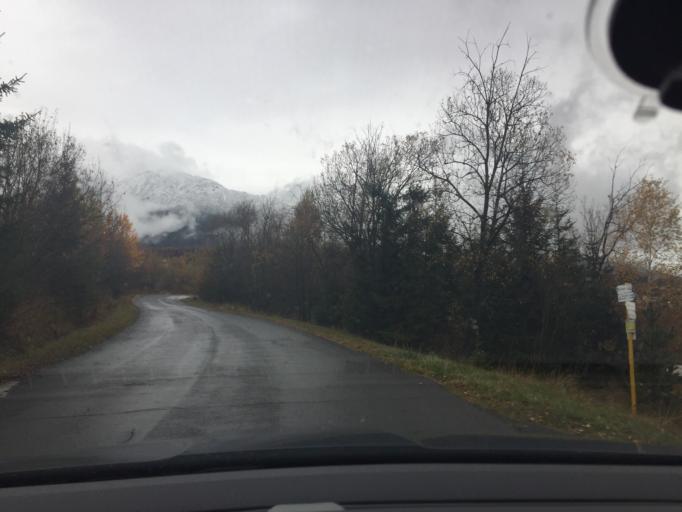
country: SK
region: Presovsky
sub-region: Okres Poprad
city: Vysoke Tatry
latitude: 49.1347
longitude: 20.2397
